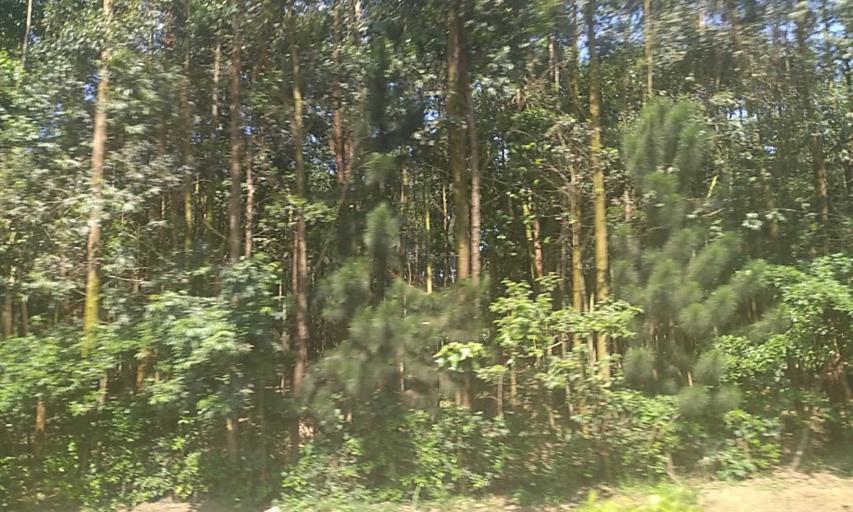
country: UG
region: Central Region
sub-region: Wakiso District
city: Kireka
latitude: 0.3612
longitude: 32.6509
